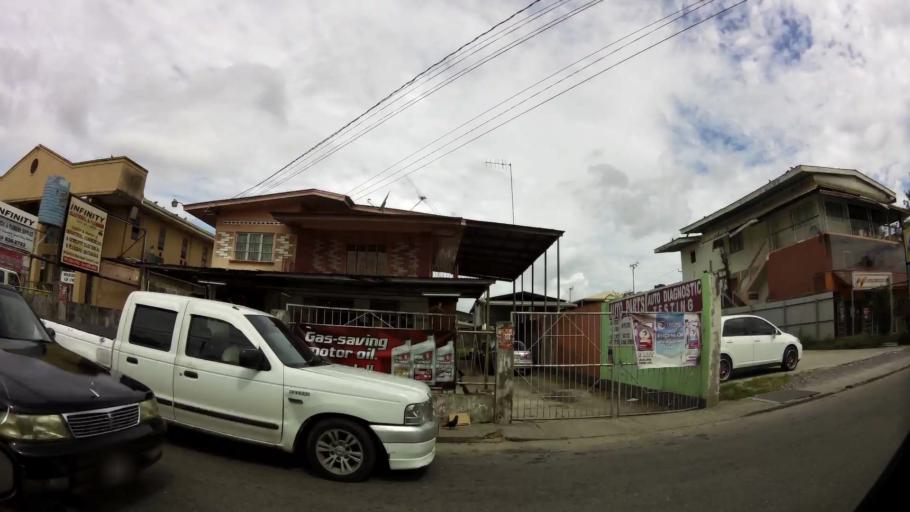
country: TT
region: Couva-Tabaquite-Talparo
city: Couva
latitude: 10.4225
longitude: -61.4699
